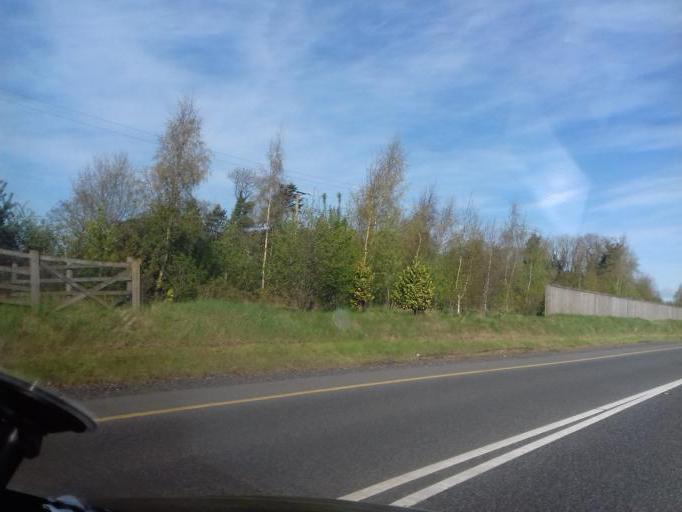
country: IE
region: Leinster
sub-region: An Mhi
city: Navan
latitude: 53.6429
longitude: -6.7446
